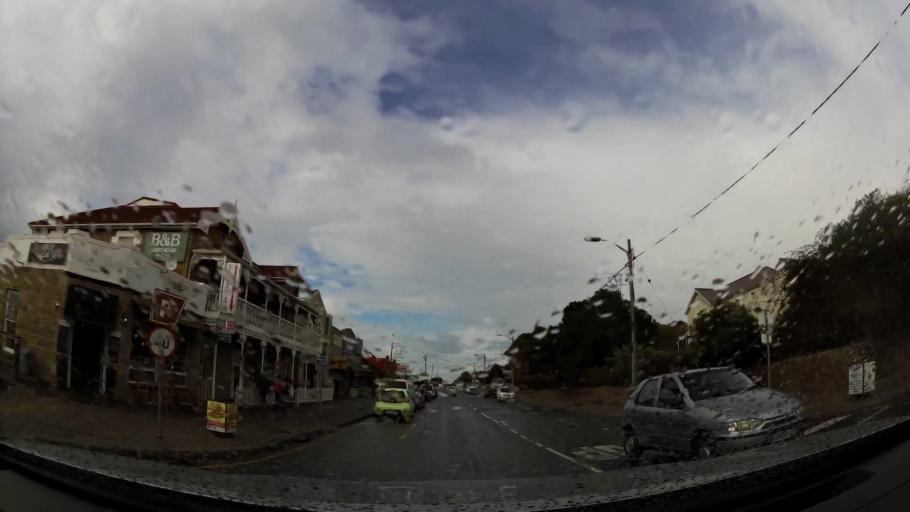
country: ZA
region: Western Cape
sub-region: Eden District Municipality
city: Mossel Bay
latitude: -34.1828
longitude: 22.1480
